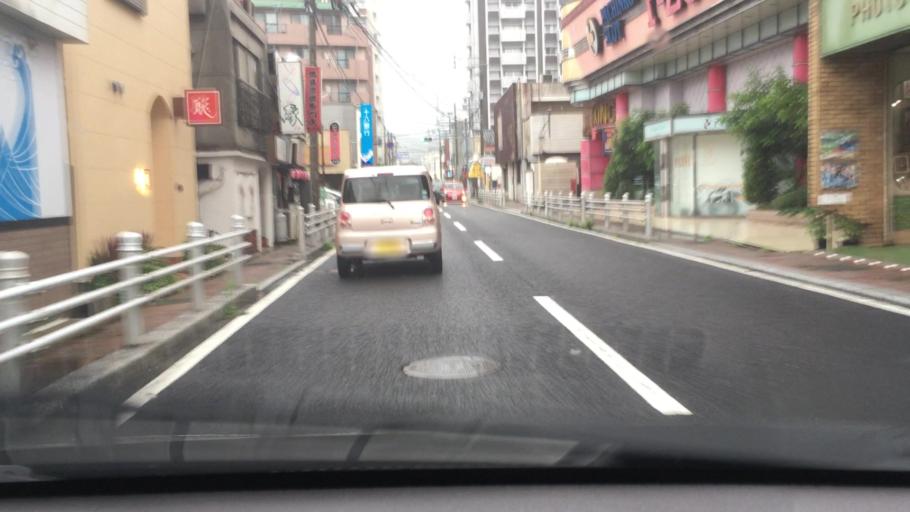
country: JP
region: Nagasaki
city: Sasebo
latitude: 33.1340
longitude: 129.7984
